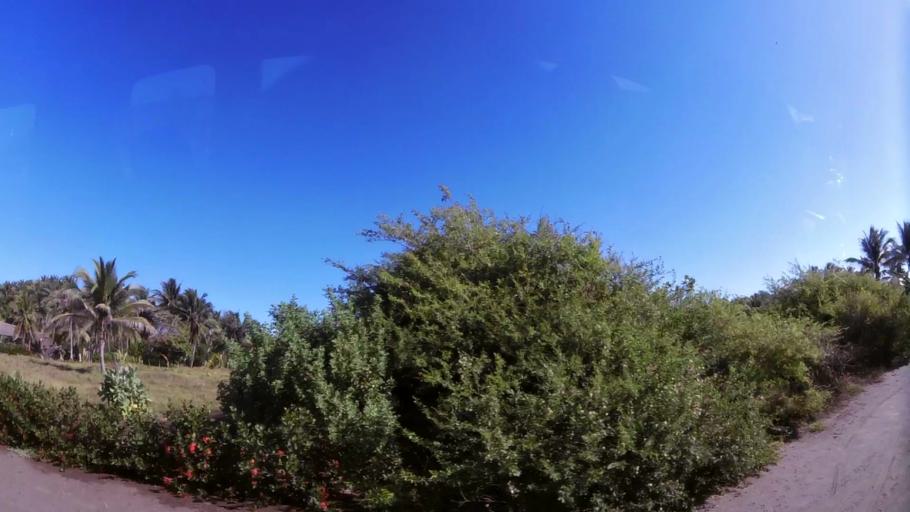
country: GT
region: Jutiapa
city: Pasaco
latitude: 13.8547
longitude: -90.3852
